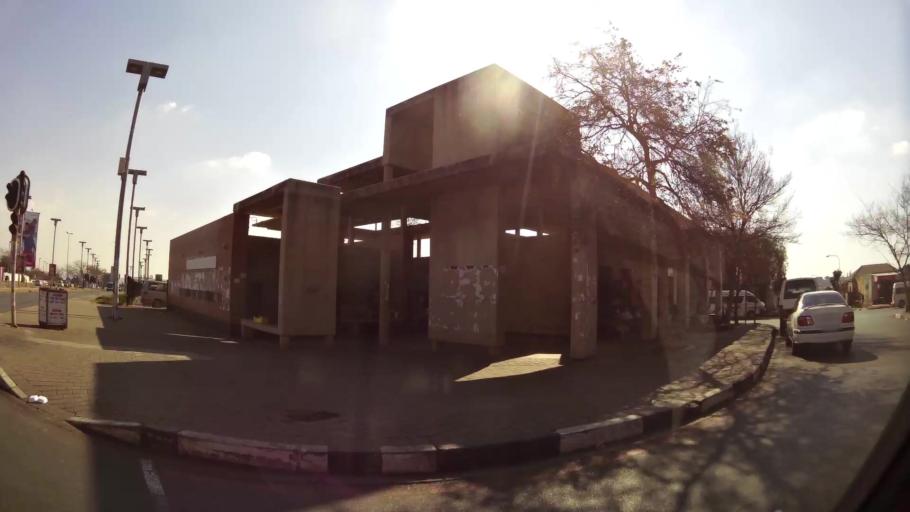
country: ZA
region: Gauteng
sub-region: City of Johannesburg Metropolitan Municipality
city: Soweto
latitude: -26.2594
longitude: 27.9371
